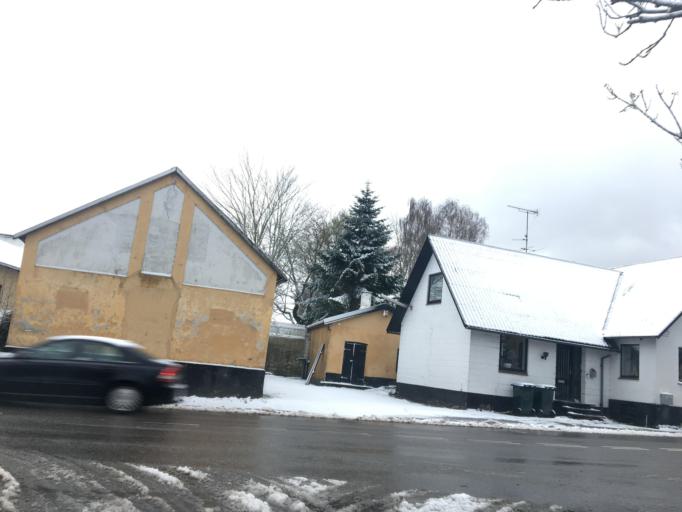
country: DK
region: Zealand
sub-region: Odsherred Kommune
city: Asnaes
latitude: 55.8375
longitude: 11.5516
